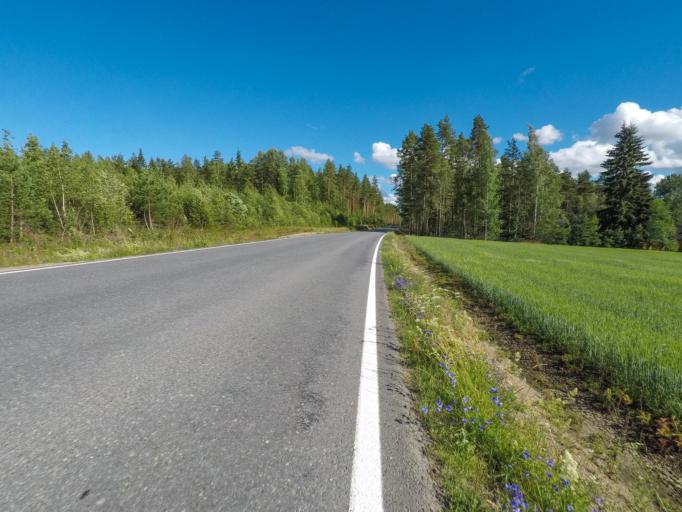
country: FI
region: South Karelia
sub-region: Lappeenranta
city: Taipalsaari
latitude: 61.1786
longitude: 28.0083
